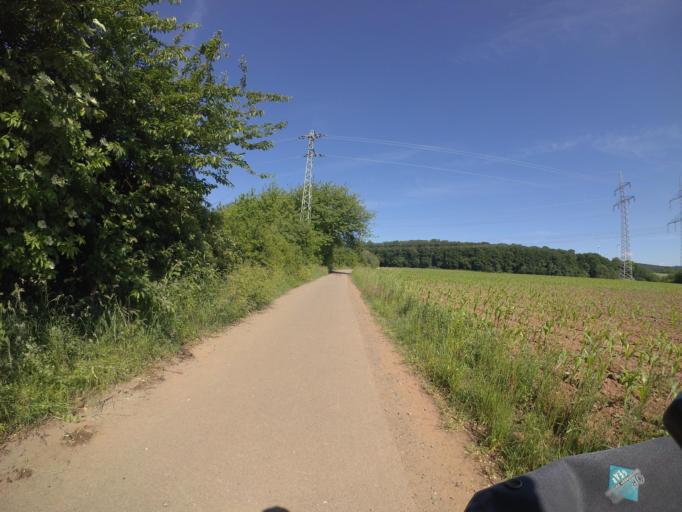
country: DE
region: Rheinland-Pfalz
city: Dunzweiler
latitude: 49.3794
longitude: 7.2901
